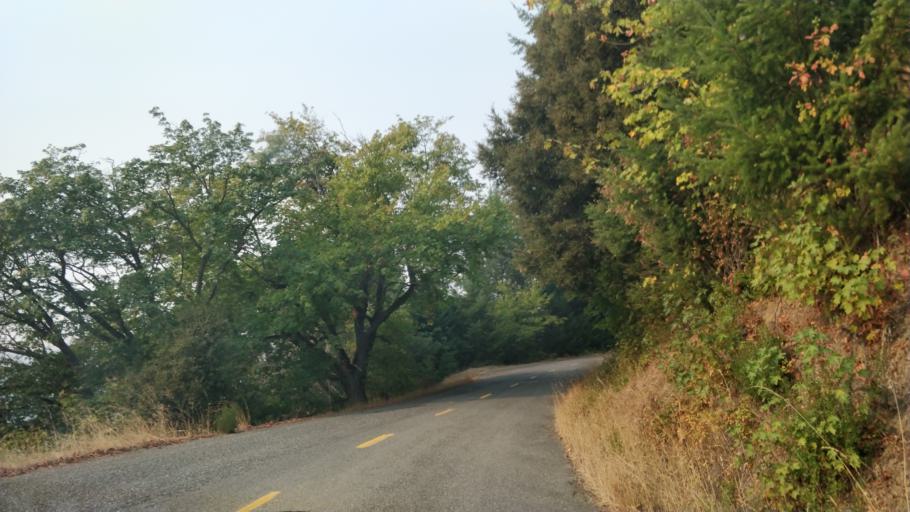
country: US
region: California
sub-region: Humboldt County
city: Rio Dell
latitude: 40.2507
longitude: -124.1252
